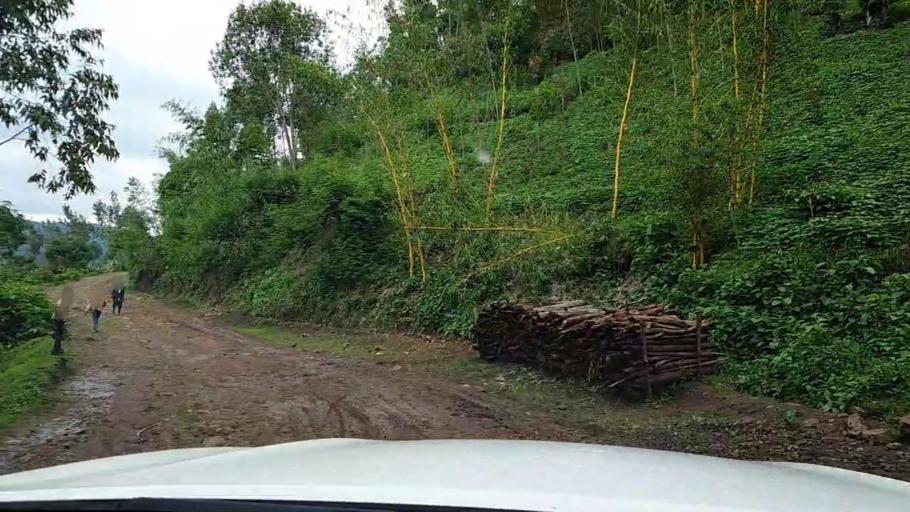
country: RW
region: Western Province
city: Cyangugu
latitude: -2.5534
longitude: 29.0364
